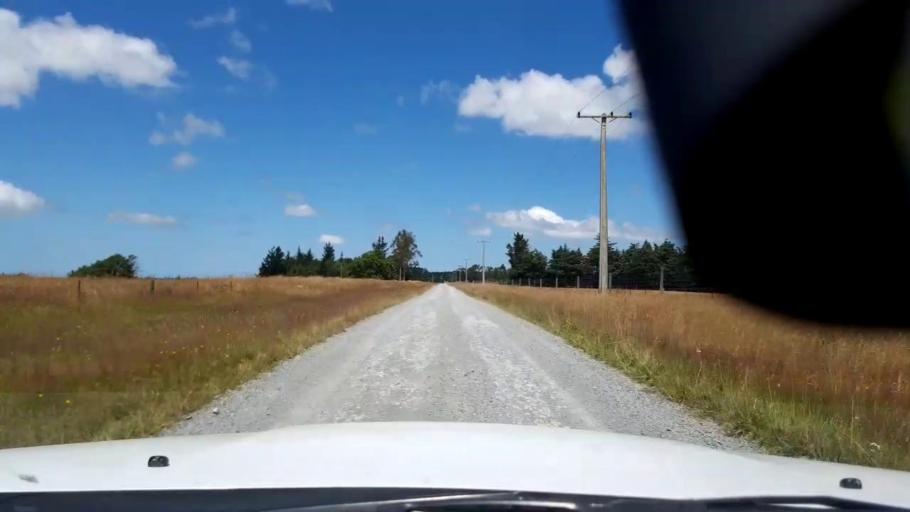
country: NZ
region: Canterbury
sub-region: Timaru District
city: Pleasant Point
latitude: -43.9859
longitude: 171.2892
